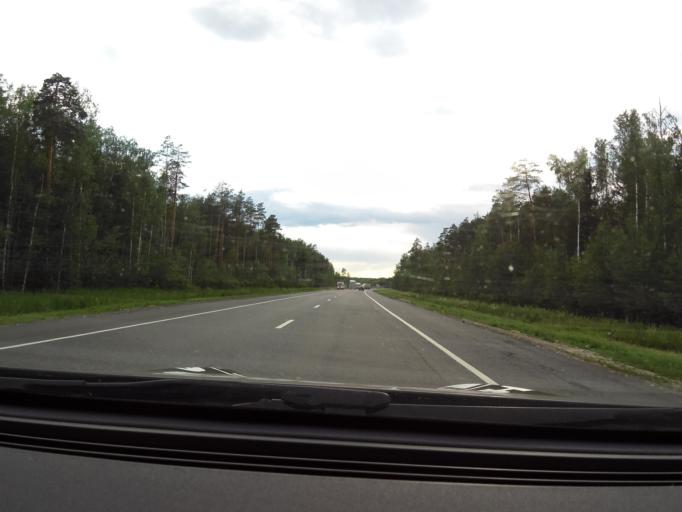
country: RU
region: Vladimir
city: Raduzhnyy
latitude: 56.0649
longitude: 40.3267
